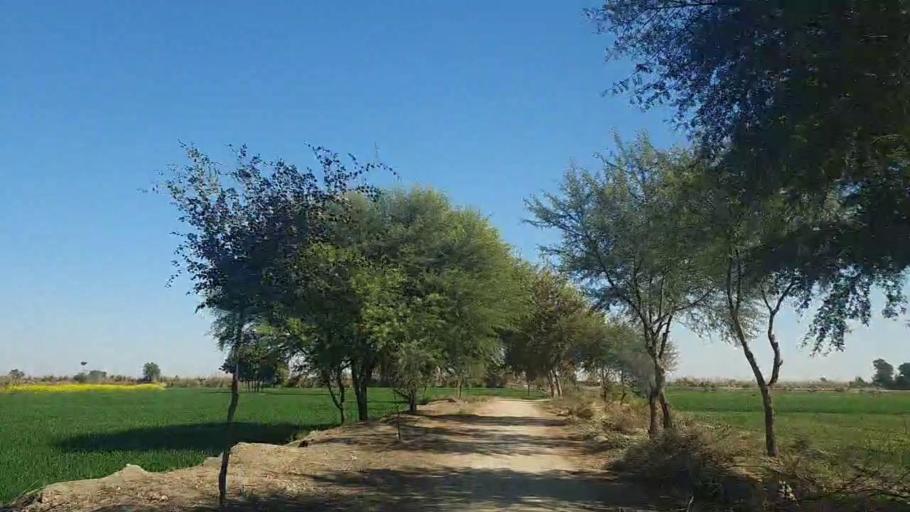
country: PK
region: Sindh
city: Khadro
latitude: 26.2180
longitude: 68.8676
